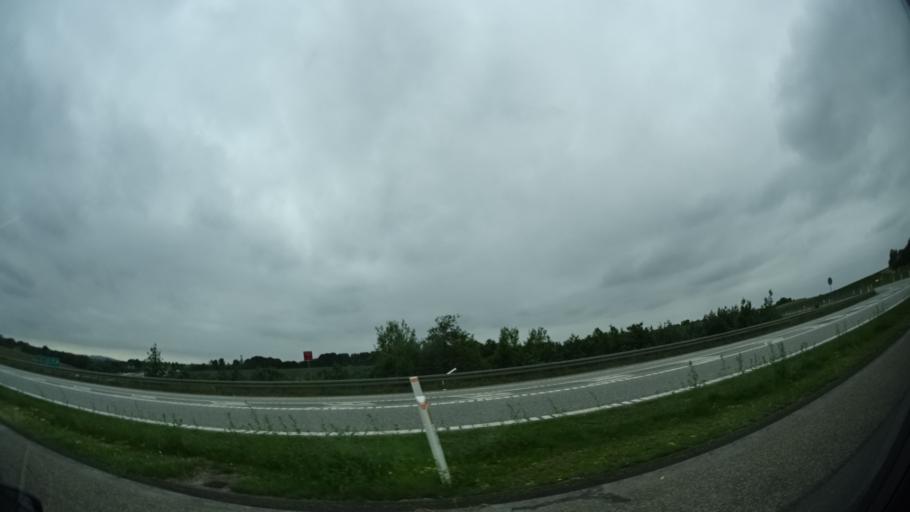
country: DK
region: Central Jutland
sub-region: Arhus Kommune
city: Framlev
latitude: 56.1579
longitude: 10.0449
